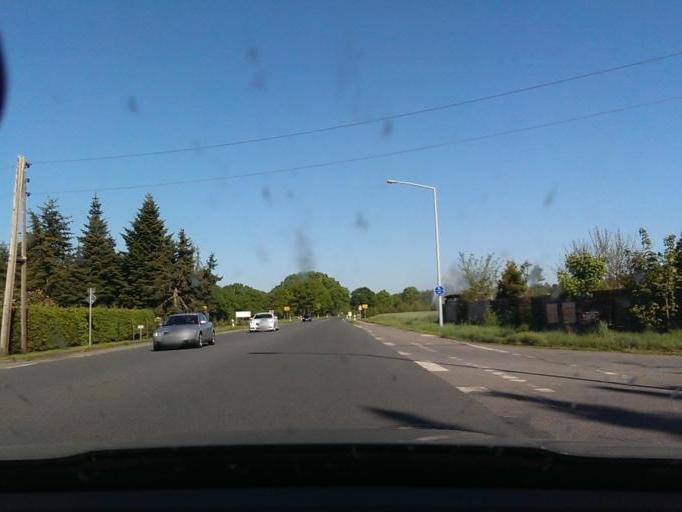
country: DE
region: Lower Saxony
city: Wietze
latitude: 52.6464
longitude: 9.8667
